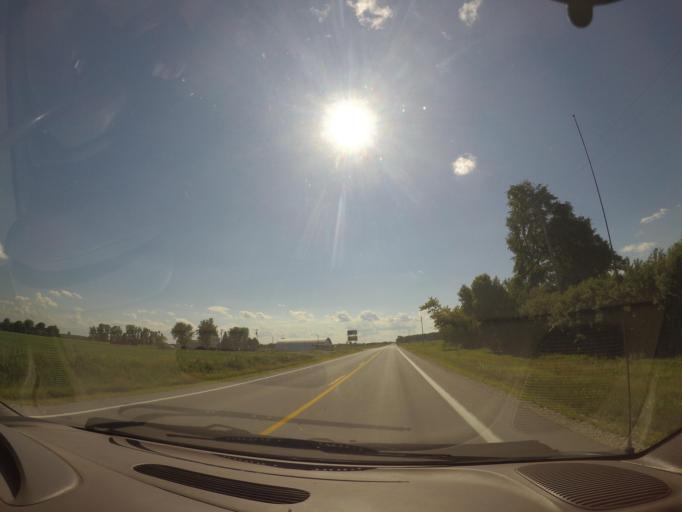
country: US
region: Ohio
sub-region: Sandusky County
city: Stony Prairie
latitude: 41.3415
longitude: -83.2231
